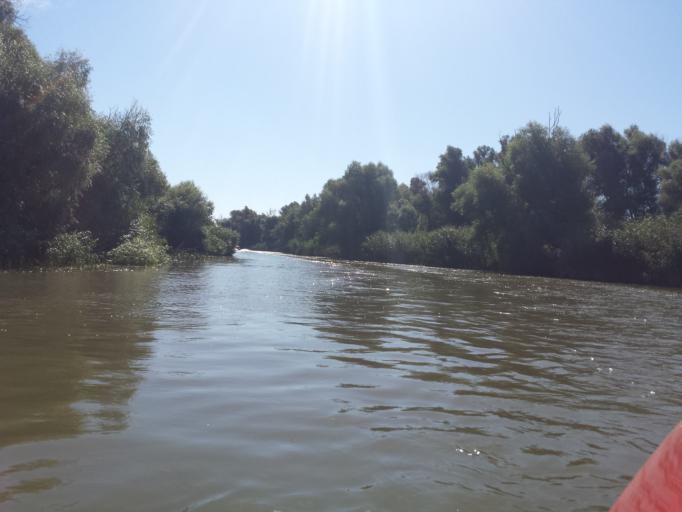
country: RO
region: Tulcea
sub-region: Comuna Pardina
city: Pardina
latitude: 45.2426
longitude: 29.0808
